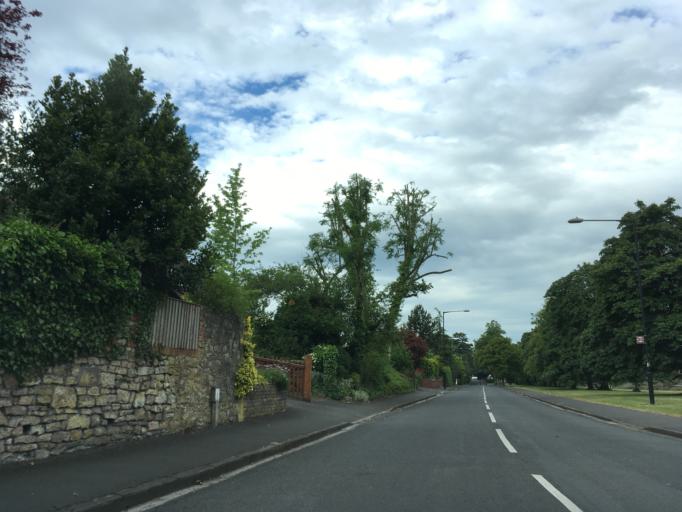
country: GB
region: England
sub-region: North Somerset
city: Long Ashton
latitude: 51.4828
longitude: -2.6451
